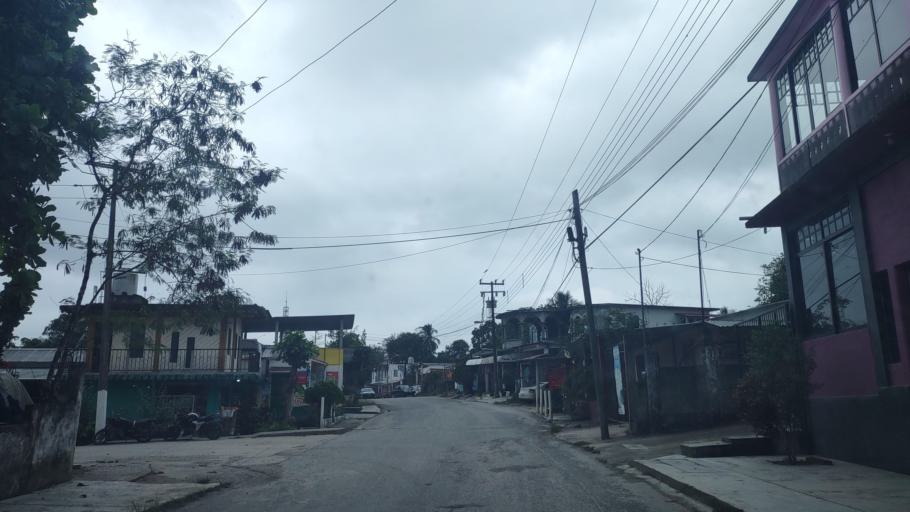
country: MX
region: Veracruz
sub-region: Uxpanapa
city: Poblado 10
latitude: 17.4988
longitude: -94.1641
